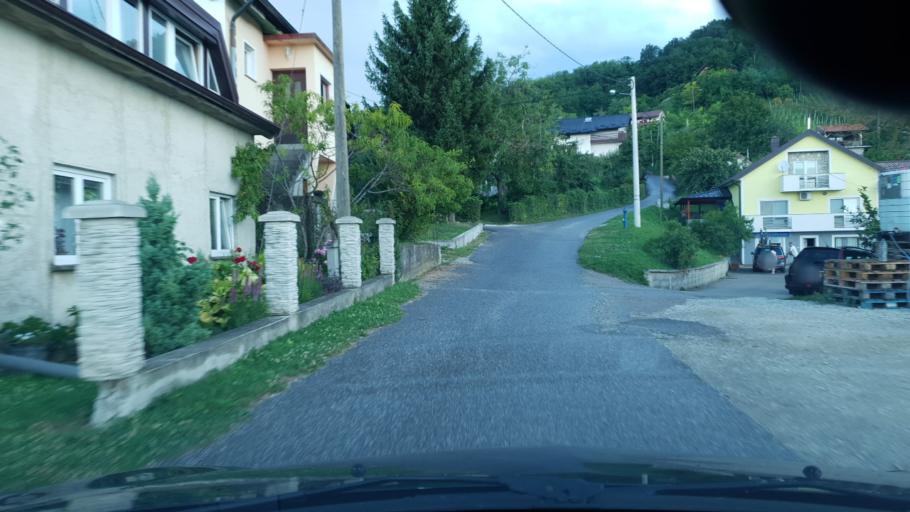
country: HR
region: Krapinsko-Zagorska
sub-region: Grad Krapina
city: Krapina
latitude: 46.1659
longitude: 15.8823
